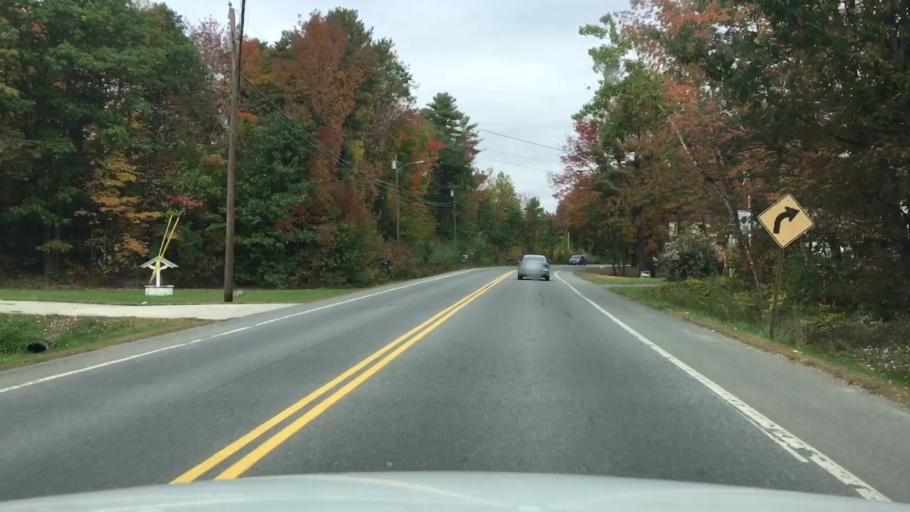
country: US
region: Maine
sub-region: Kennebec County
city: Waterville
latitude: 44.5488
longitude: -69.6767
